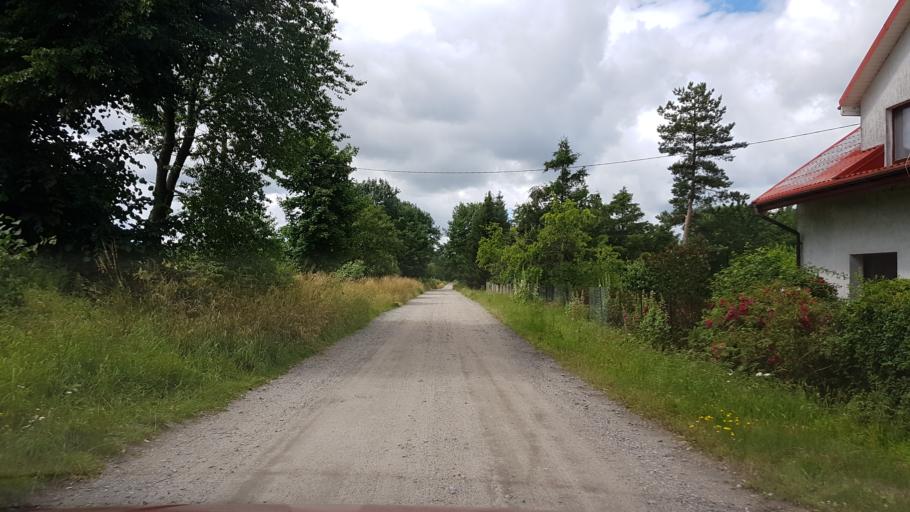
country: PL
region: West Pomeranian Voivodeship
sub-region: Powiat bialogardzki
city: Karlino
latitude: 54.1639
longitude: 15.9378
